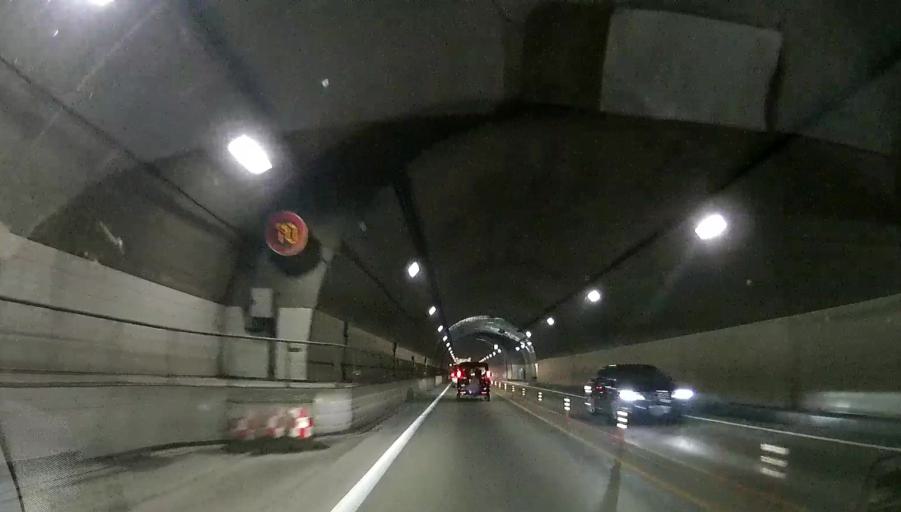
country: JP
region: Hokkaido
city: Shimo-furano
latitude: 43.0567
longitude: 142.5066
